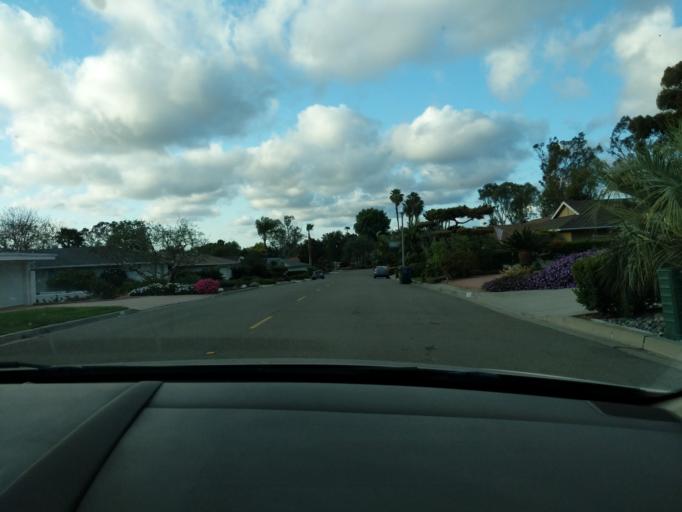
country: US
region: California
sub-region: San Diego County
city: Lake San Marcos
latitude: 33.1223
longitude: -117.2002
